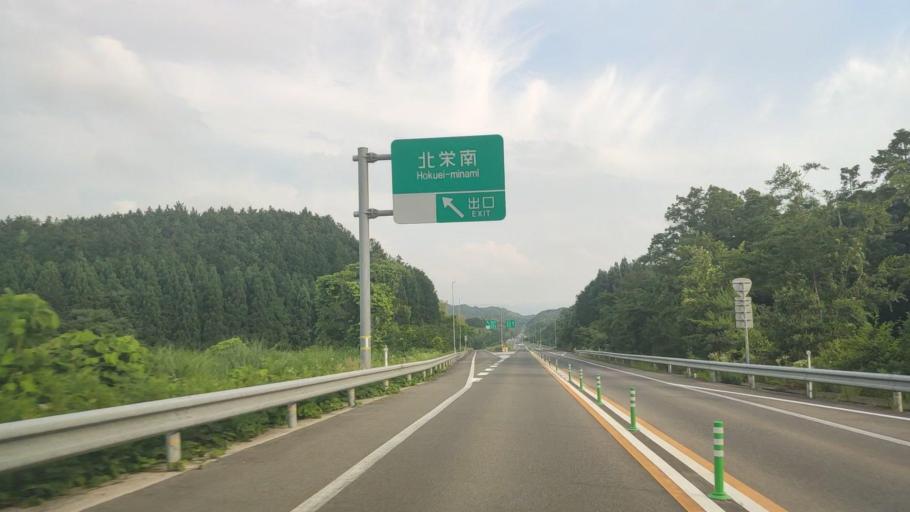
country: JP
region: Tottori
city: Kurayoshi
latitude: 35.4696
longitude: 133.8076
